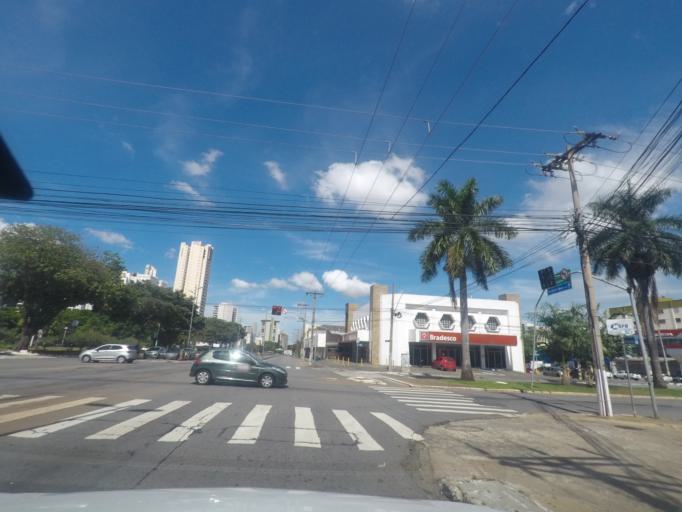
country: BR
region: Goias
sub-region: Goiania
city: Goiania
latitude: -16.6775
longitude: -49.2675
